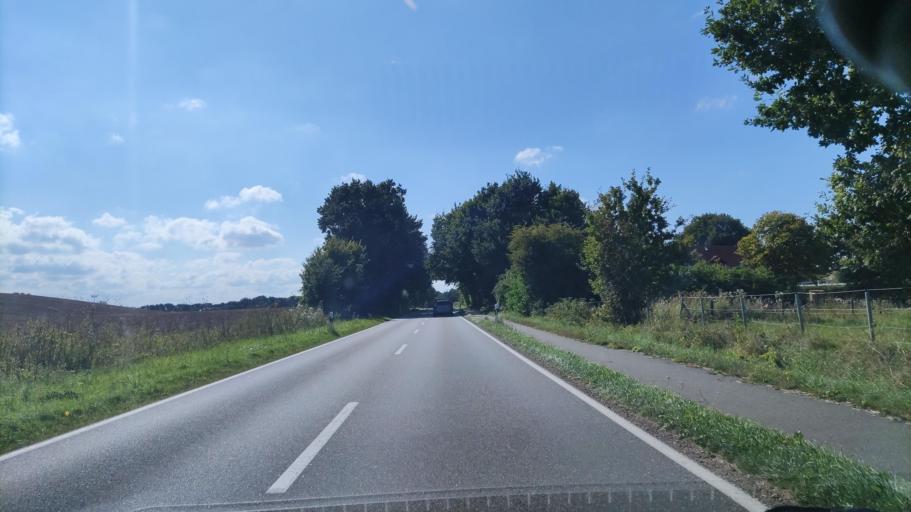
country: DE
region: Schleswig-Holstein
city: Osterby
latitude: 54.4482
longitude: 9.7496
